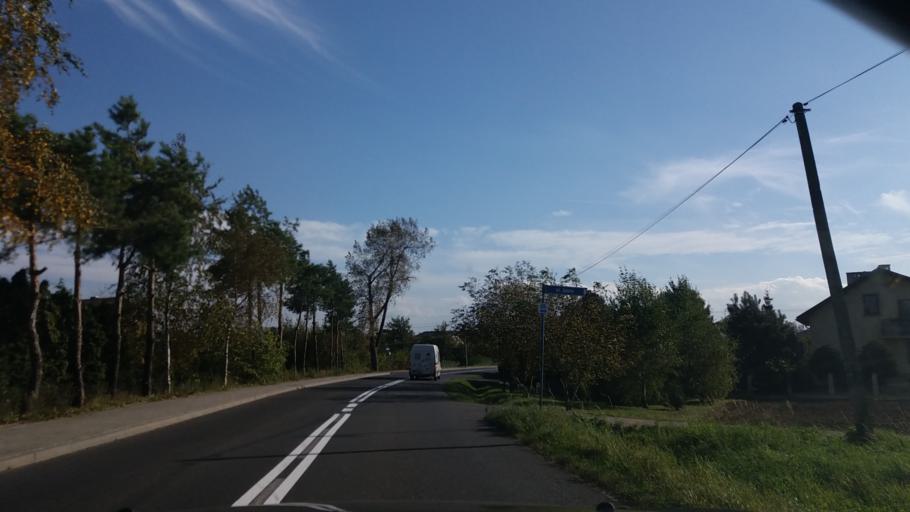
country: PL
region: Lesser Poland Voivodeship
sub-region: Powiat chrzanowski
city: Grojec
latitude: 50.0941
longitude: 19.5560
